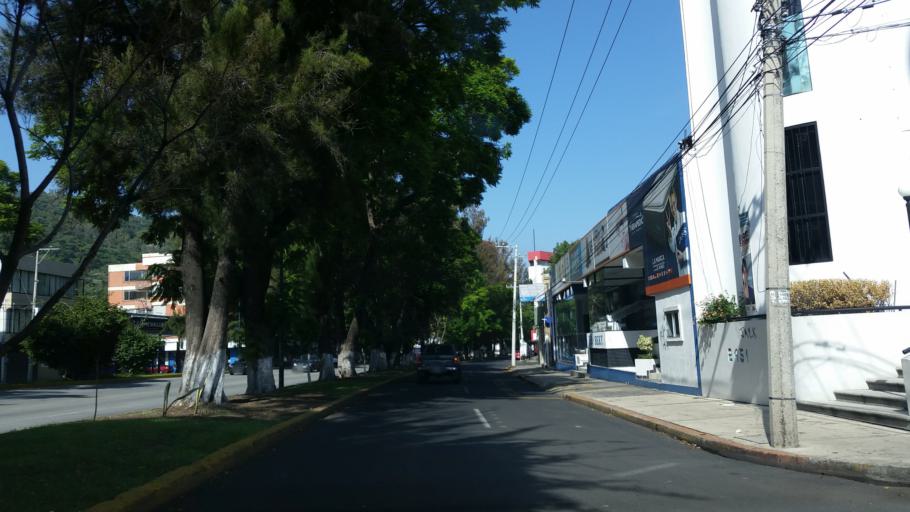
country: MX
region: Michoacan
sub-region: Morelia
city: Montana Monarca (Punta Altozano)
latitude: 19.6828
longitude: -101.1681
